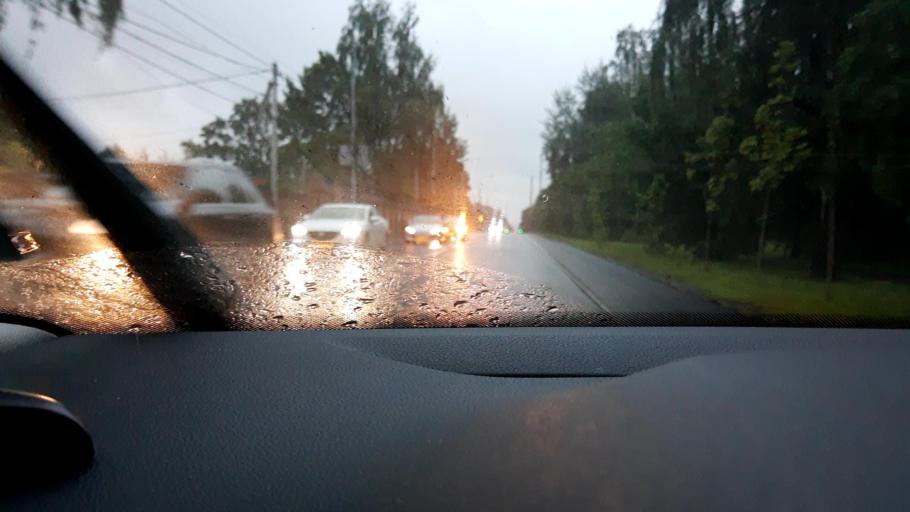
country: RU
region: Moscow
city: Khimki
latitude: 55.8863
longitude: 37.3830
